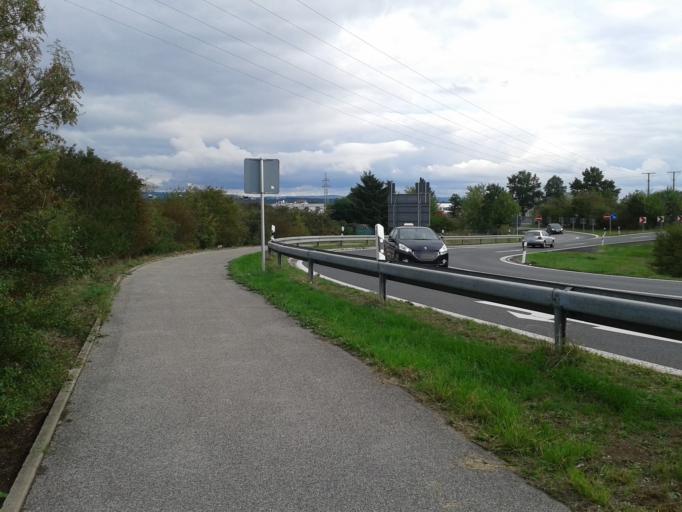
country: DE
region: Bavaria
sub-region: Upper Franconia
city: Gundelsheim
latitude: 49.9243
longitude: 10.8995
